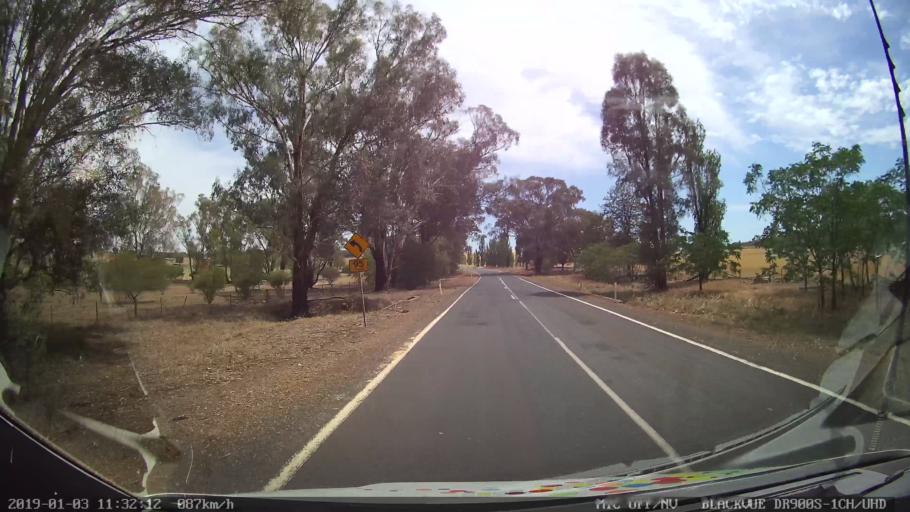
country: AU
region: New South Wales
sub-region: Weddin
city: Grenfell
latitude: -33.9614
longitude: 148.1797
